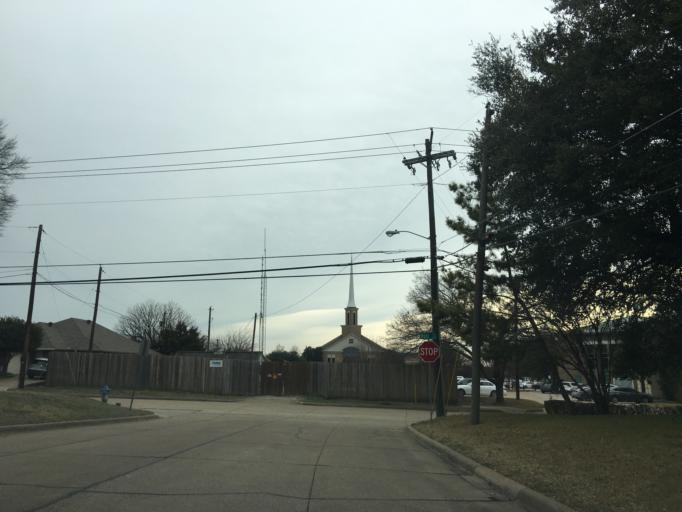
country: US
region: Texas
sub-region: Collin County
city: McKinney
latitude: 33.1996
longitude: -96.6318
